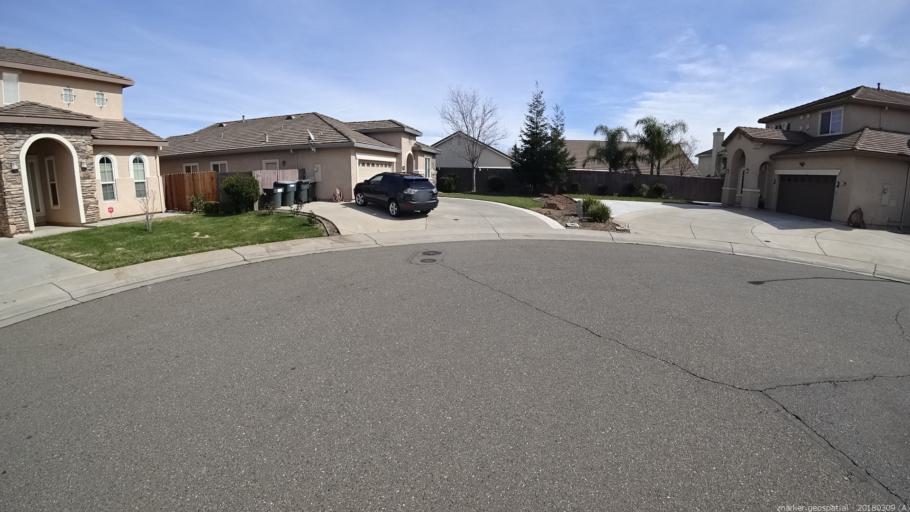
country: US
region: California
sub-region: Sacramento County
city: Vineyard
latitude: 38.4570
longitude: -121.3614
